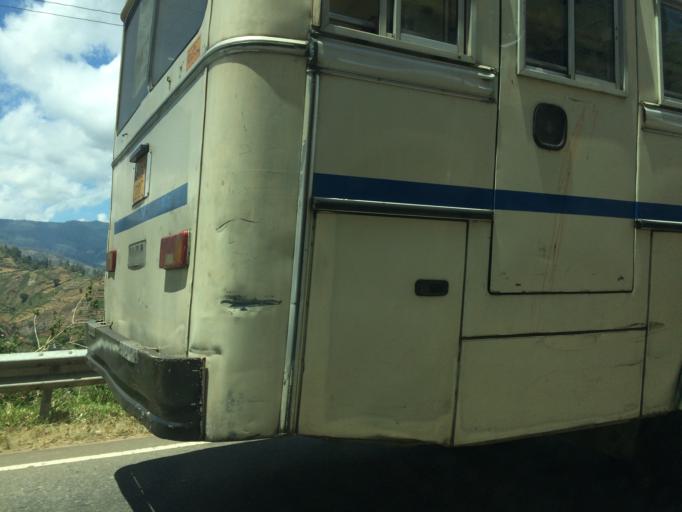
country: LK
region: Central
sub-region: Nuwara Eliya District
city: Nuwara Eliya
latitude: 6.9066
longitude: 80.8503
